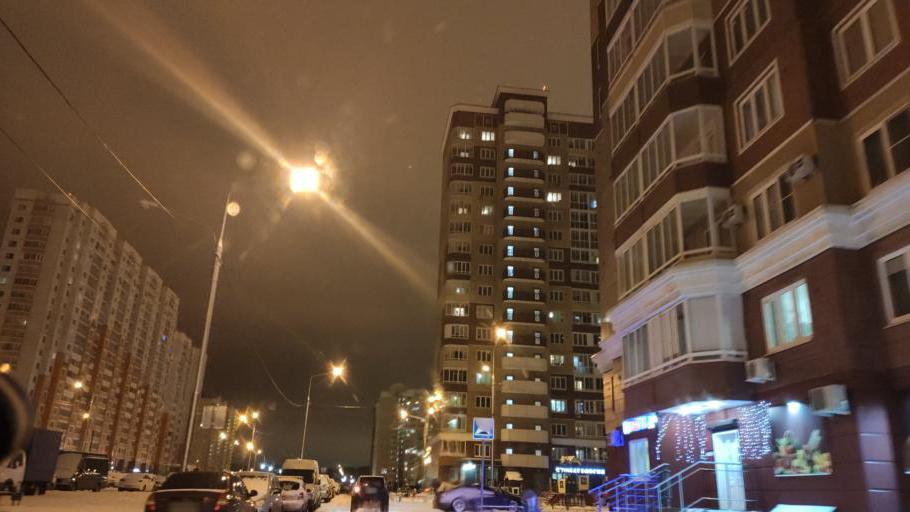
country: RU
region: Moskovskaya
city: Shcherbinka
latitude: 55.5242
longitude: 37.5930
